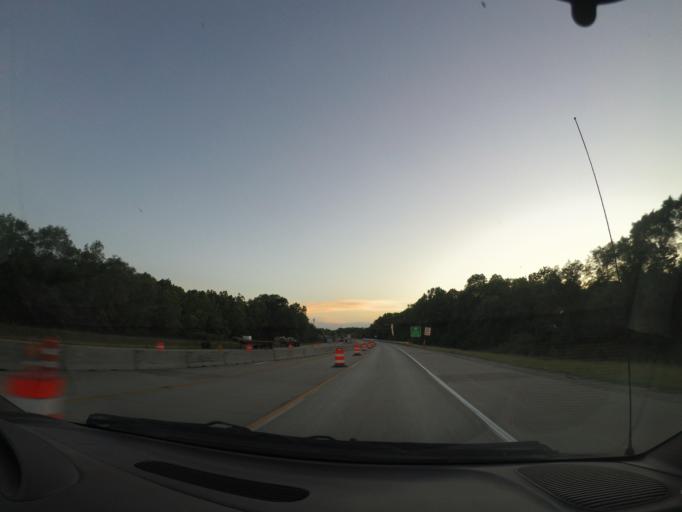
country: US
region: Indiana
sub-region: Elkhart County
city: Dunlap
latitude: 41.6570
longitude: -85.9284
